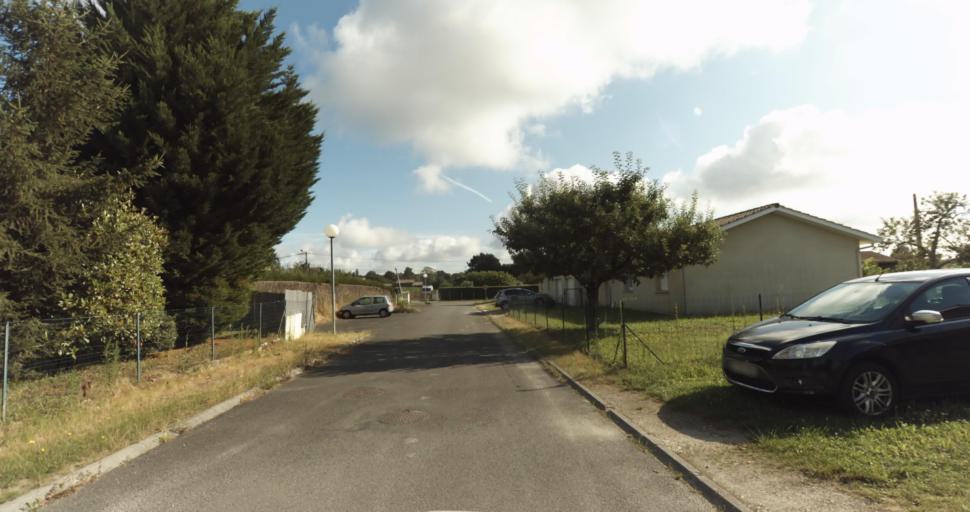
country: FR
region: Aquitaine
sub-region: Departement de la Gironde
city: Bazas
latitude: 44.4338
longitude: -0.2438
